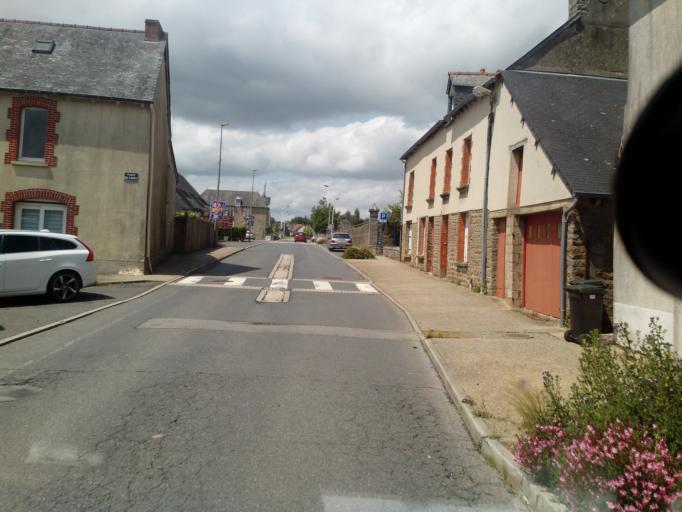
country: FR
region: Brittany
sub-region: Departement des Cotes-d'Armor
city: Merdrignac
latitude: 48.1939
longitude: -2.4155
